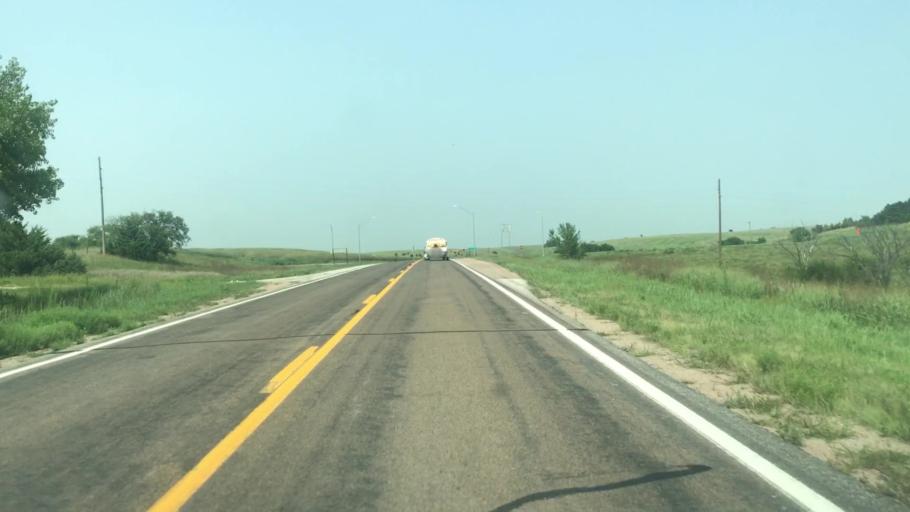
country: US
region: Nebraska
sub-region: Sherman County
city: Loup City
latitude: 41.2606
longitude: -98.9388
